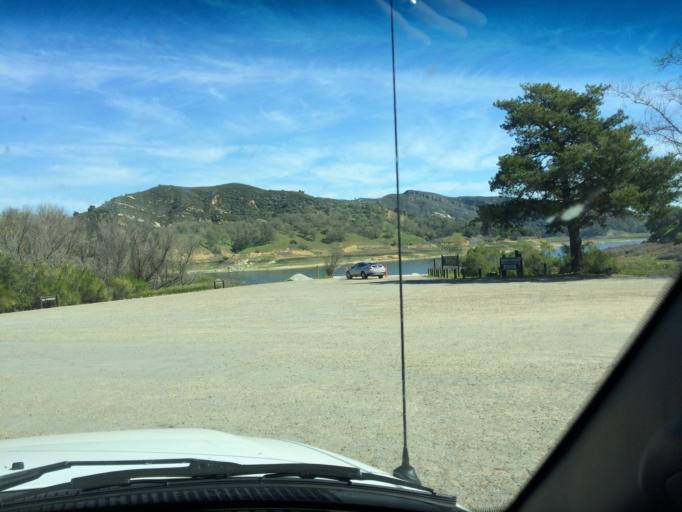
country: US
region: California
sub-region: San Luis Obispo County
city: Santa Margarita
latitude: 35.3272
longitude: -120.4912
